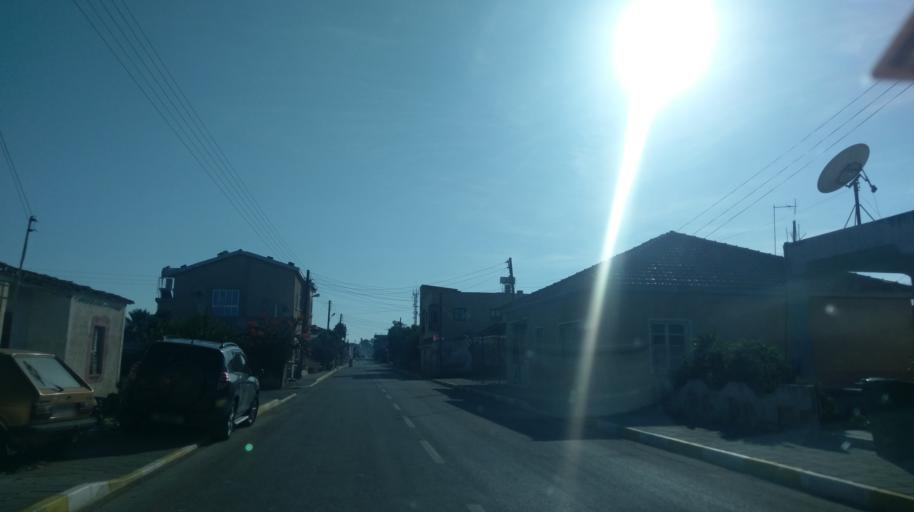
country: CY
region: Larnaka
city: Pergamos
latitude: 35.0438
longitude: 33.7084
